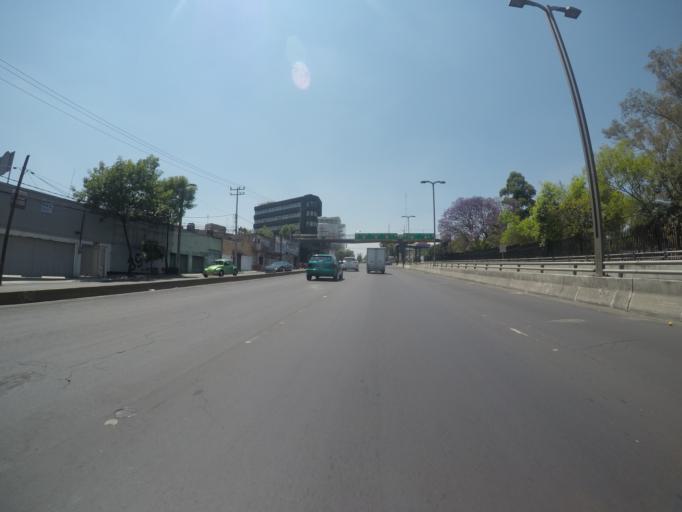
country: MX
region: Mexico City
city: Polanco
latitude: 19.4067
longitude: -99.2019
